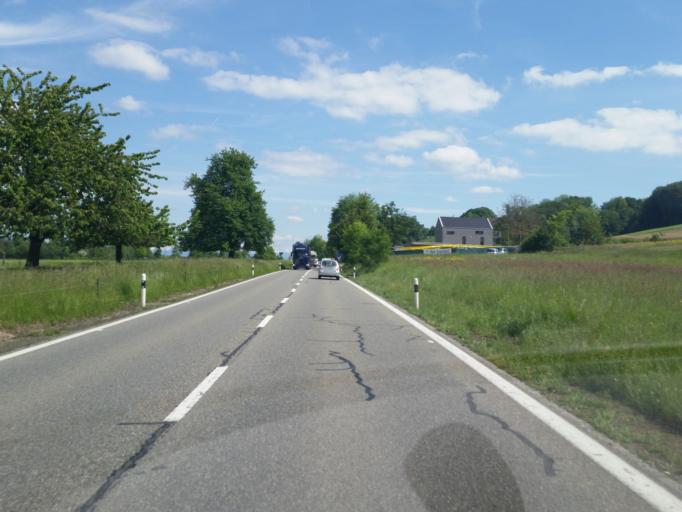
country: CH
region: Aargau
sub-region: Bezirk Muri
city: Waltenschwil
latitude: 47.3297
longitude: 8.2859
